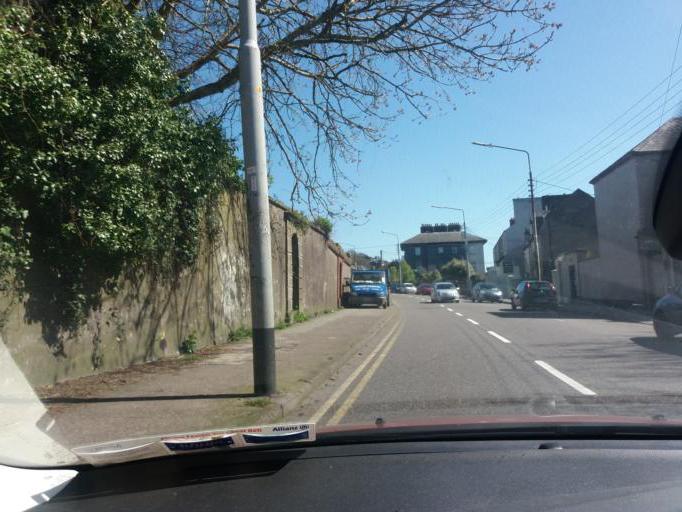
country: IE
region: Munster
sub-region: County Cork
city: Cork
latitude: 51.9033
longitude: -8.4591
